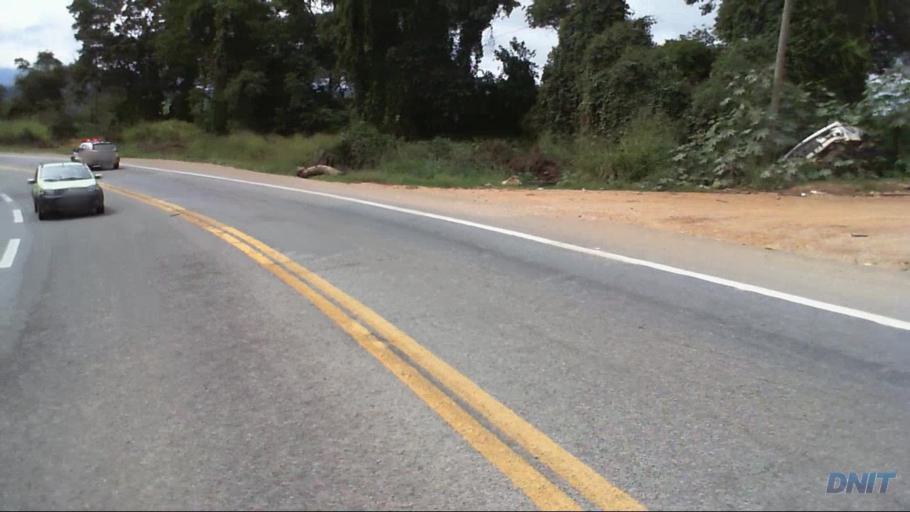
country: BR
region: Minas Gerais
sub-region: Caete
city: Caete
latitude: -19.7567
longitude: -43.6314
